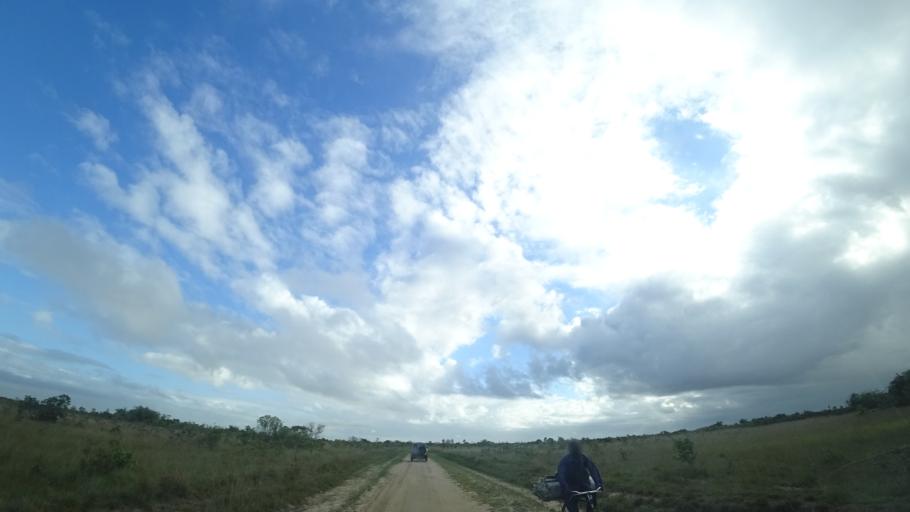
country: MZ
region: Sofala
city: Beira
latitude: -19.6755
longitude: 35.0592
